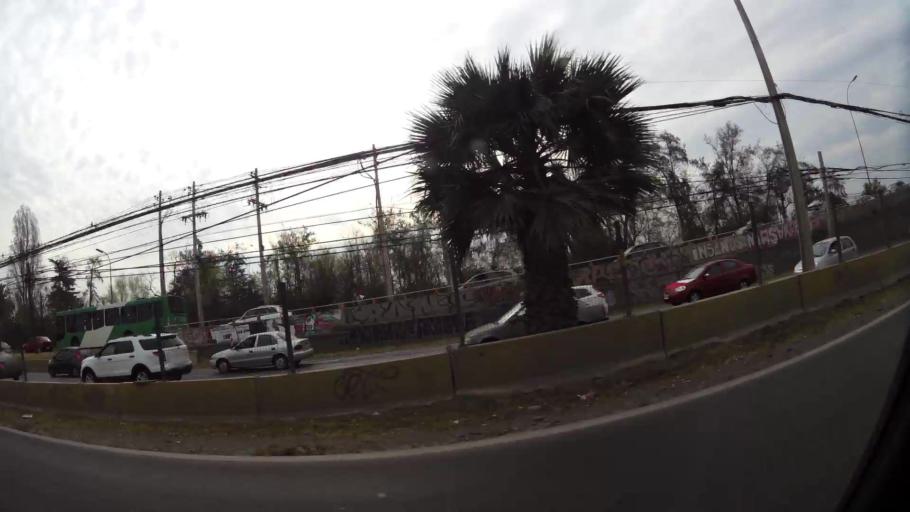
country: CL
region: Santiago Metropolitan
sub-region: Provincia de Maipo
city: San Bernardo
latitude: -33.5285
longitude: -70.7584
